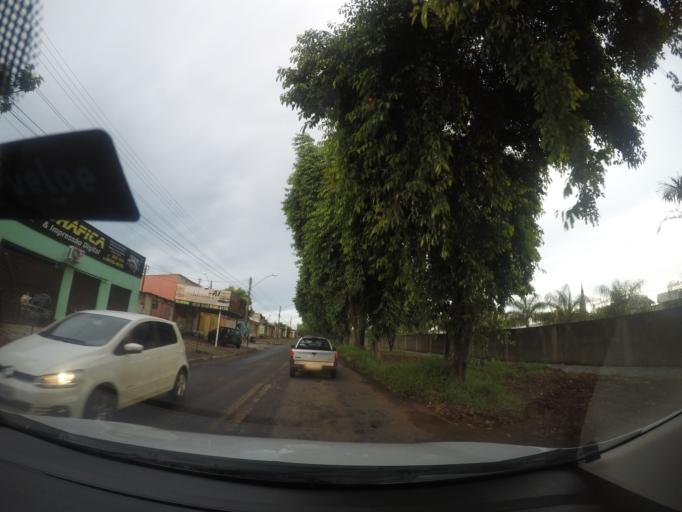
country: BR
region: Goias
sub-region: Goiania
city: Goiania
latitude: -16.7241
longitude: -49.3100
